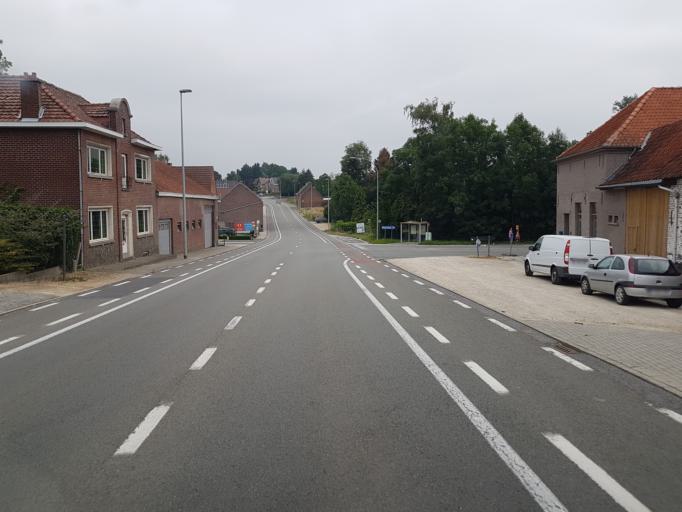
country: BE
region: Flanders
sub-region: Provincie Oost-Vlaanderen
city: Haaltert
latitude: 50.8589
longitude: 3.9599
